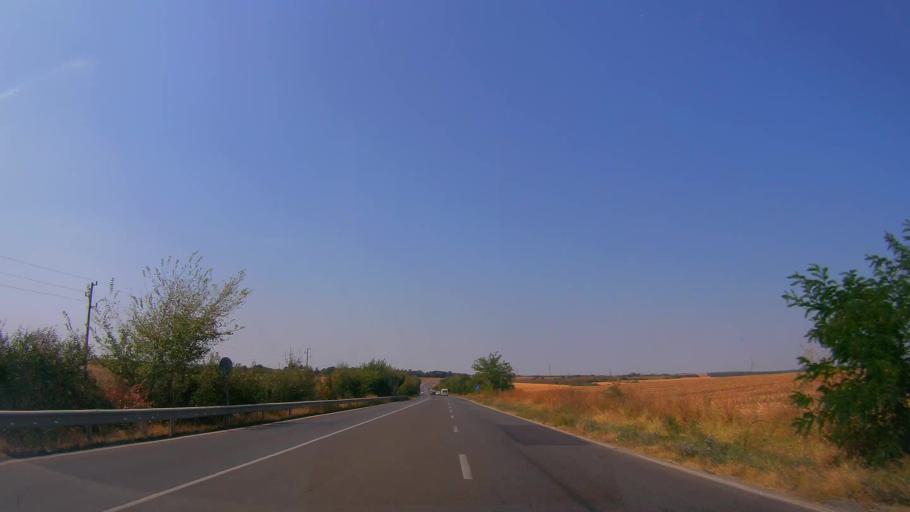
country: BG
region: Ruse
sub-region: Obshtina Vetovo
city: Senovo
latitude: 43.5659
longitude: 26.3320
